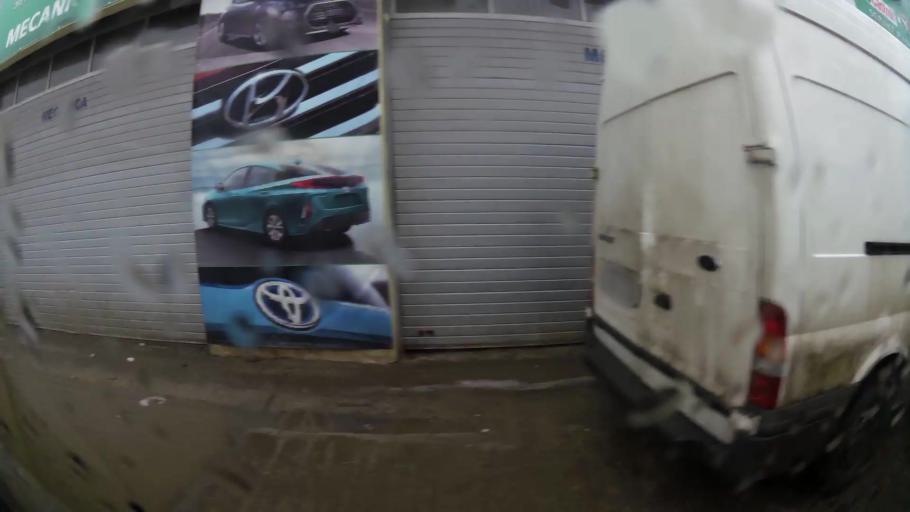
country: RO
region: Ilfov
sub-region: Comuna Chiajna
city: Rosu
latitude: 44.4300
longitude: 26.0079
